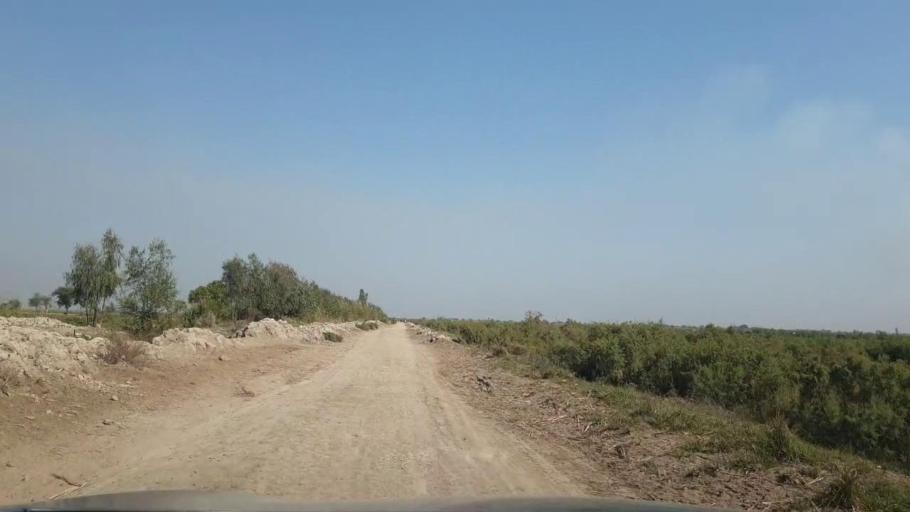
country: PK
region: Sindh
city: Berani
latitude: 25.6509
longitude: 68.8779
